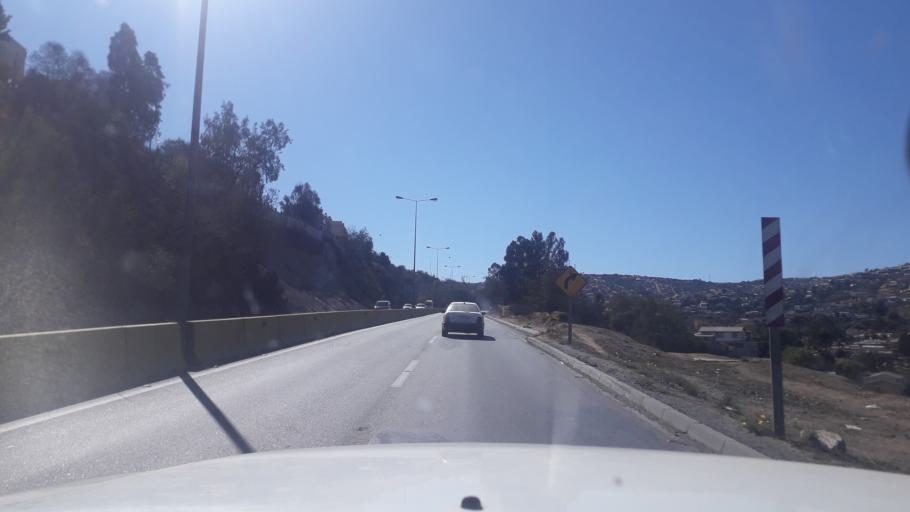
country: CL
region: Valparaiso
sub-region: Provincia de Valparaiso
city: Vina del Mar
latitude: -33.0335
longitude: -71.5011
